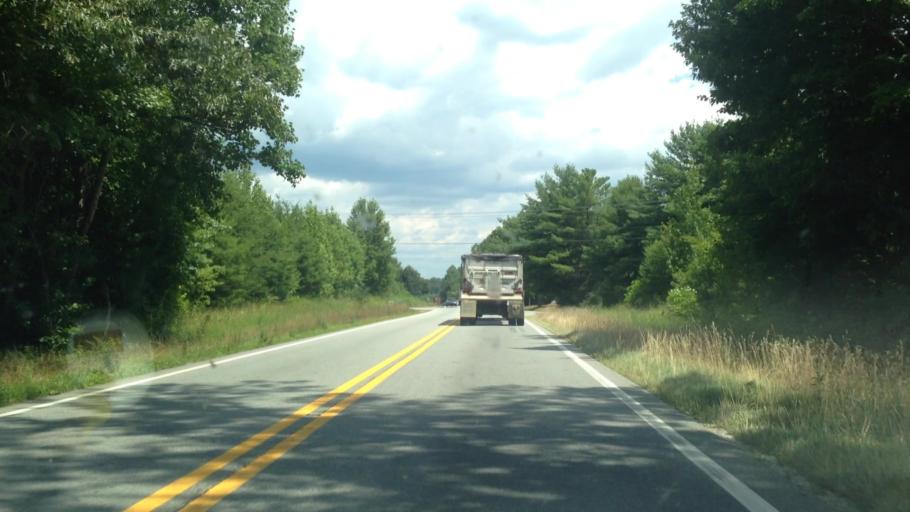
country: US
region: North Carolina
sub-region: Guilford County
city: Stokesdale
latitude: 36.2745
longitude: -79.9437
